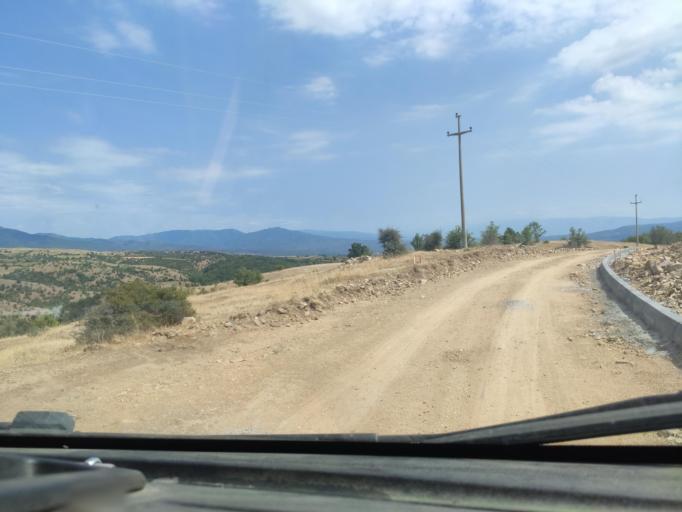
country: MK
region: Radovis
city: Radovish
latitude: 41.6682
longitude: 22.4061
